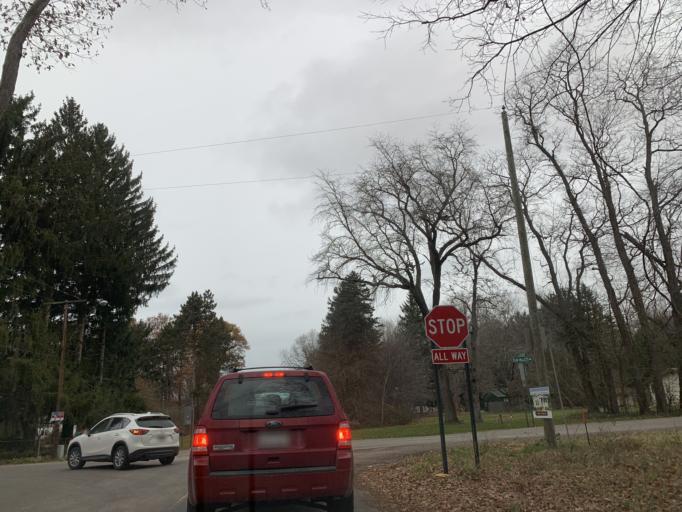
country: US
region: Michigan
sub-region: Berrien County
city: Three Oaks
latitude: 41.8277
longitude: -86.6682
